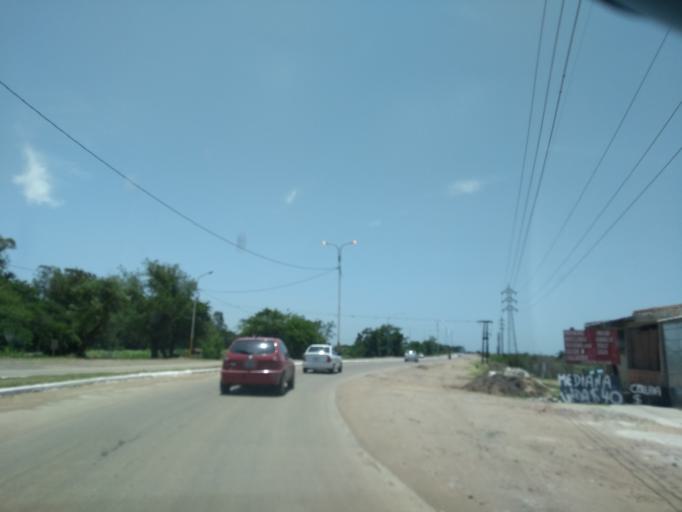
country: AR
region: Chaco
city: Barranqueras
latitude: -27.4635
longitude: -58.9145
